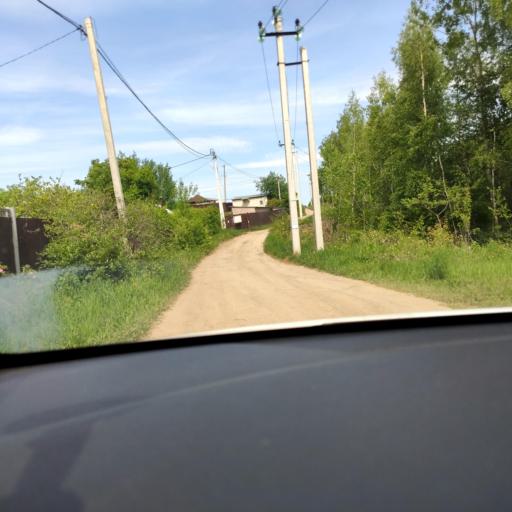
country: RU
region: Tatarstan
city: Vysokaya Gora
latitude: 55.9938
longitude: 49.3268
